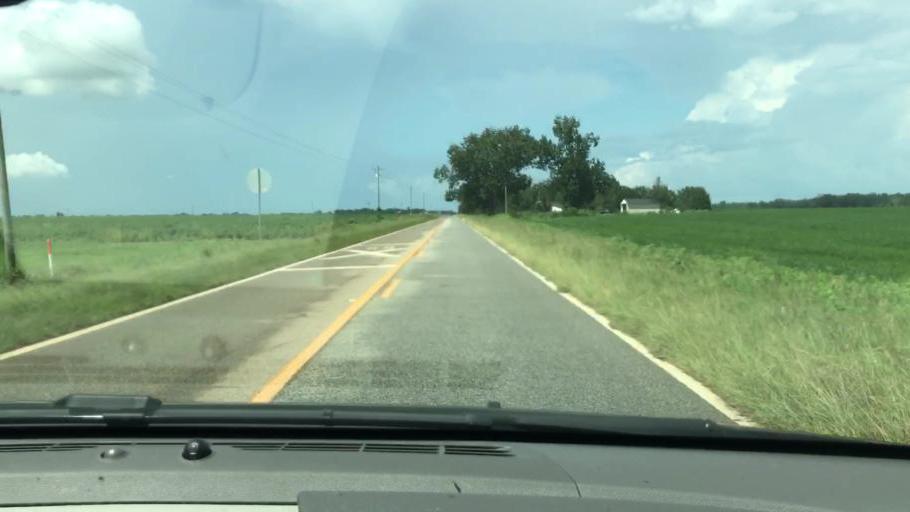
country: US
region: Georgia
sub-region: Seminole County
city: Donalsonville
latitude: 31.0938
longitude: -84.9962
